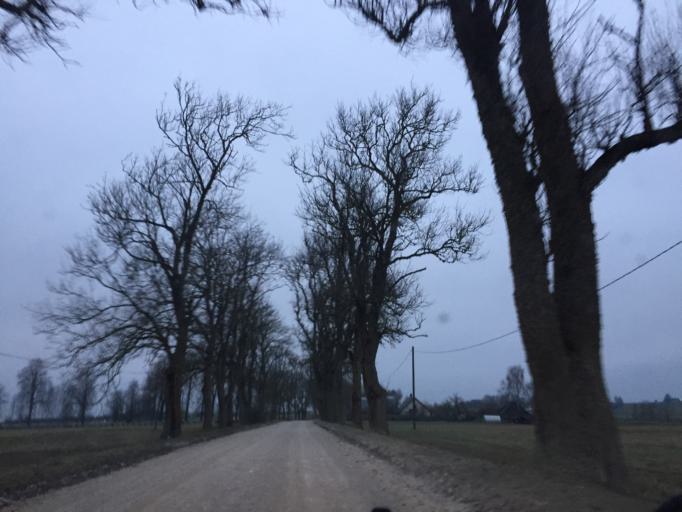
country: LV
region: Raunas
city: Rauna
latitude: 57.3400
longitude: 25.5912
